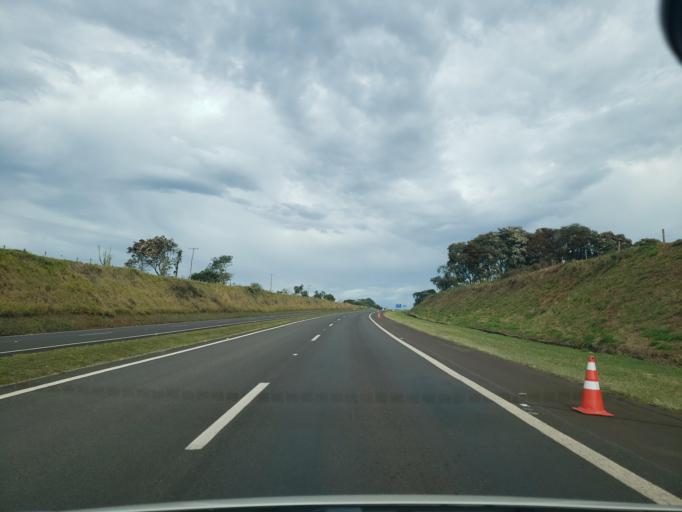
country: BR
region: Sao Paulo
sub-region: Dois Corregos
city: Dois Corregos
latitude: -22.2577
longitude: -48.3669
